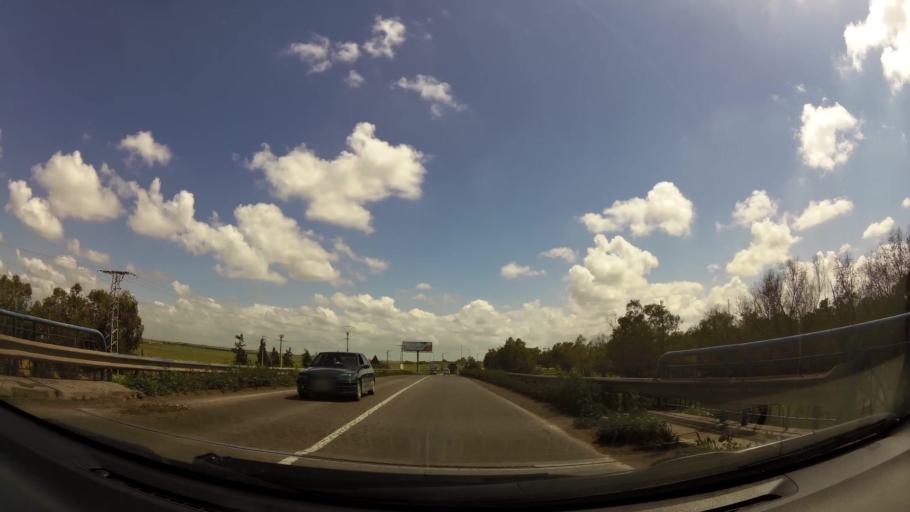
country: MA
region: Grand Casablanca
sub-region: Nouaceur
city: Dar Bouazza
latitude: 33.4212
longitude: -7.8120
